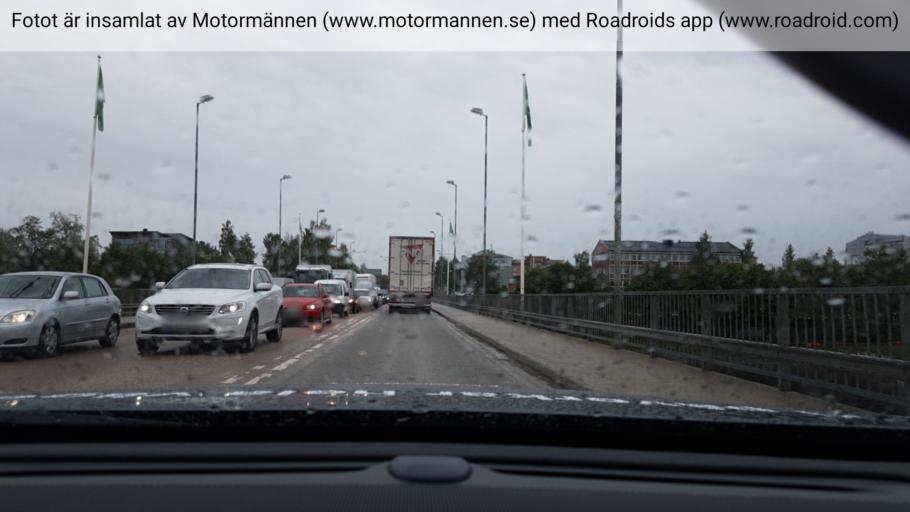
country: SE
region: Vaesterbotten
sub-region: Umea Kommun
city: Umea
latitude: 63.8241
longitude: 20.2547
